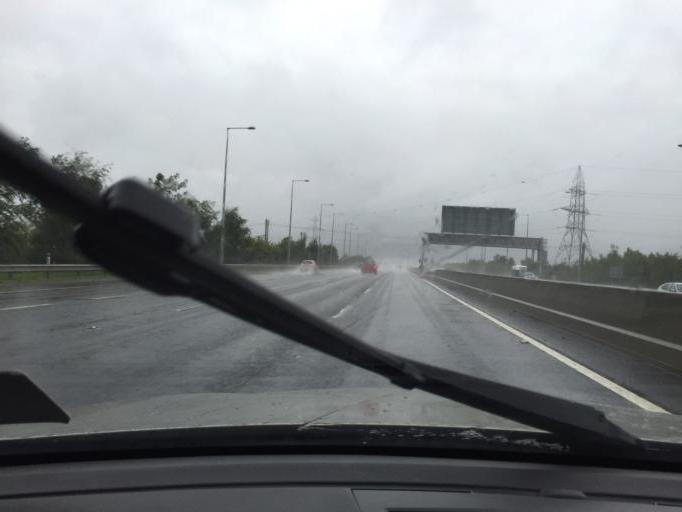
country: IE
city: Cherry Orchard
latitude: 53.3295
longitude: -6.3789
